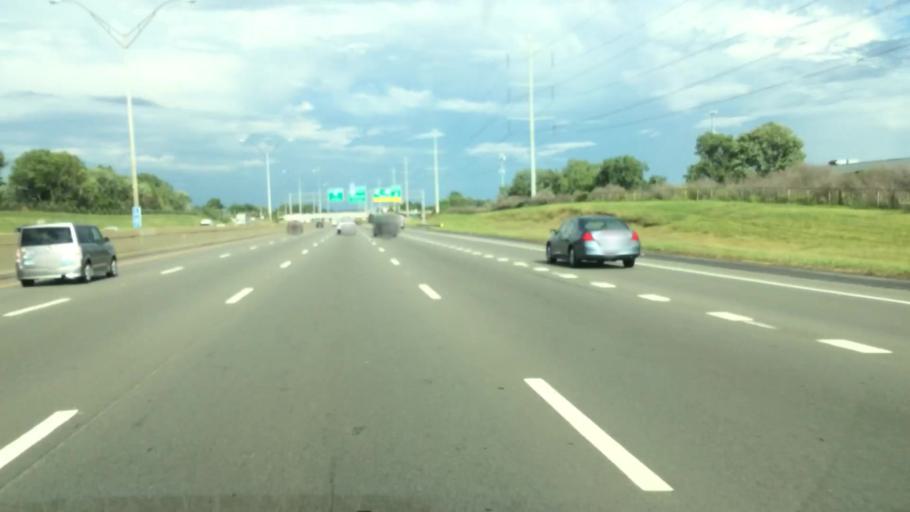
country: US
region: Ohio
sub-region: Cuyahoga County
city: Parma
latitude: 41.4216
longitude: -81.7255
